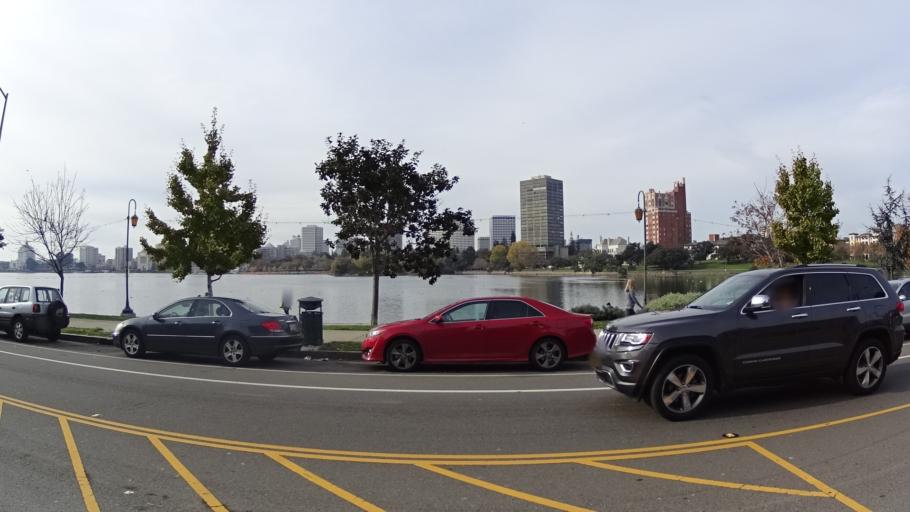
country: US
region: California
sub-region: Alameda County
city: Oakland
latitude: 37.8057
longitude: -122.2502
